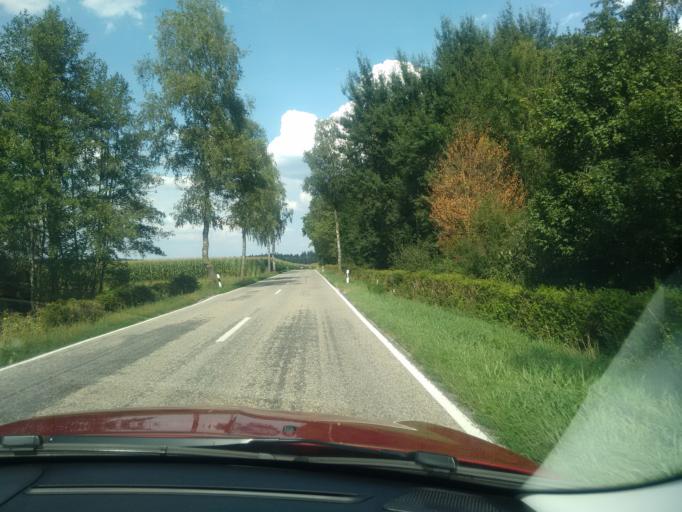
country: DE
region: Bavaria
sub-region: Upper Bavaria
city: Tyrlaching
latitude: 48.1016
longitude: 12.6666
